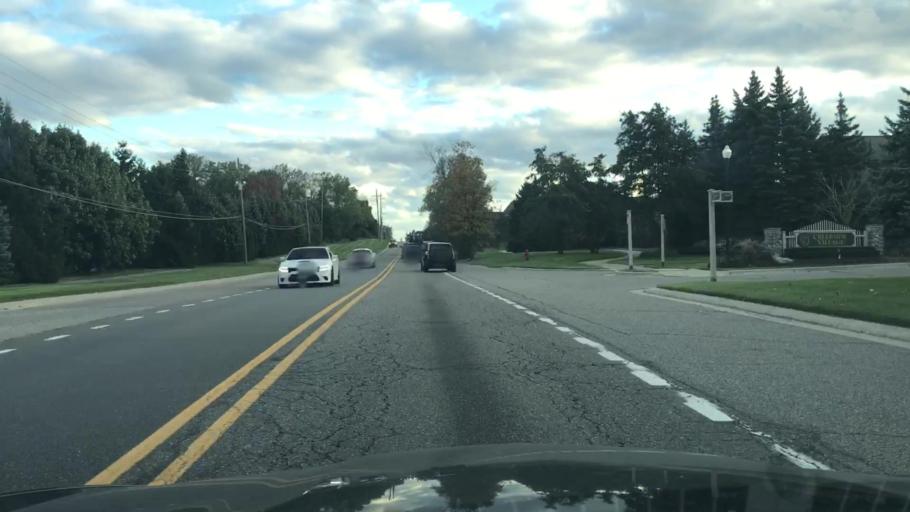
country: US
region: Michigan
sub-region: Oakland County
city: Rochester
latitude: 42.6938
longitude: -83.0949
